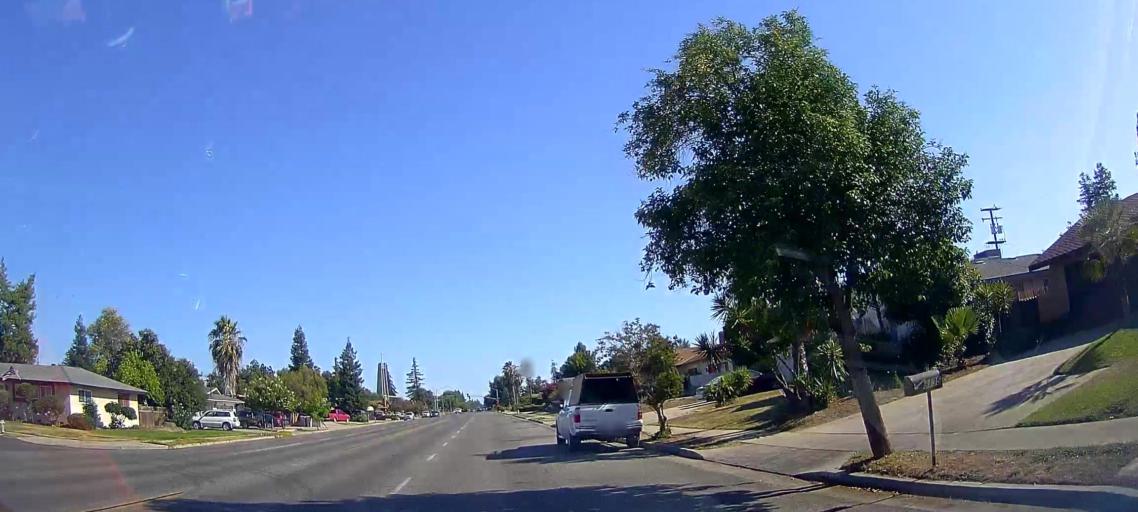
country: US
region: California
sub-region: Fresno County
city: Fresno
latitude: 36.8253
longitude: -119.7994
